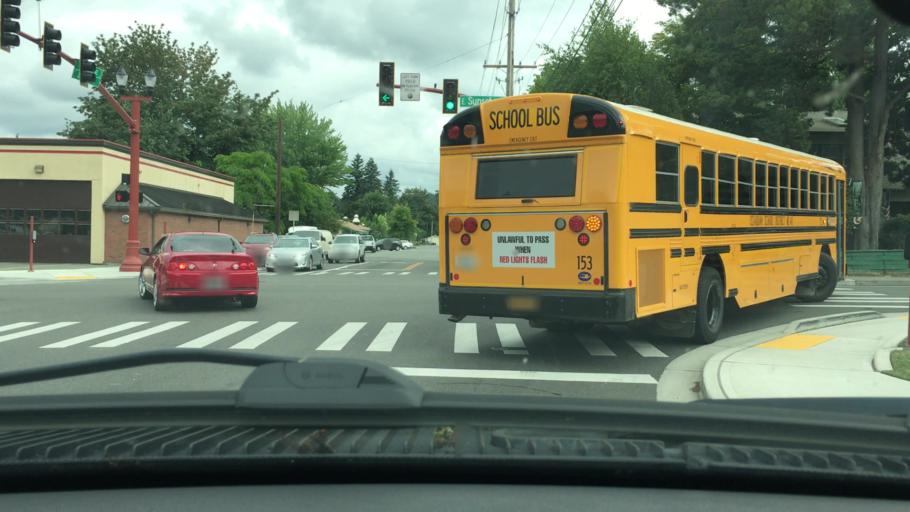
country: US
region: Washington
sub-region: King County
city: Issaquah
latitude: 47.5299
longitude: -122.0329
